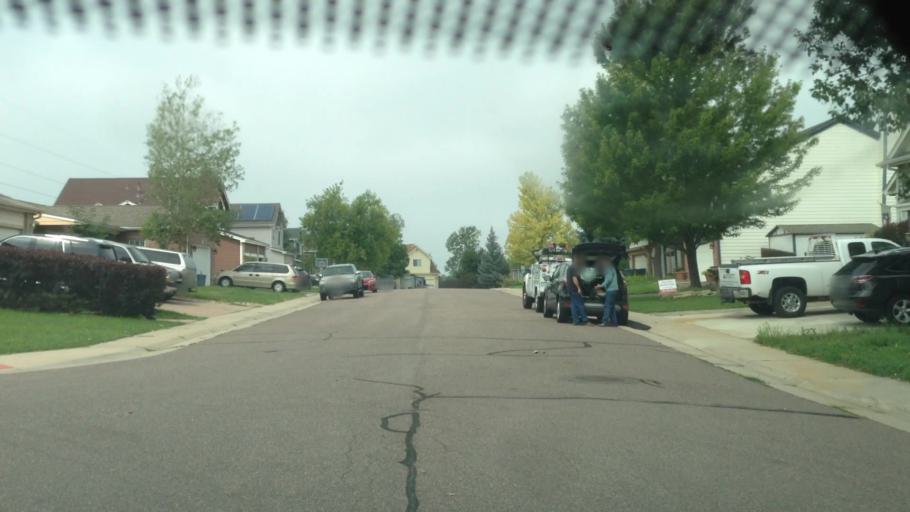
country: US
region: Colorado
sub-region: Douglas County
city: Parker
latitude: 39.6098
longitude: -104.7332
